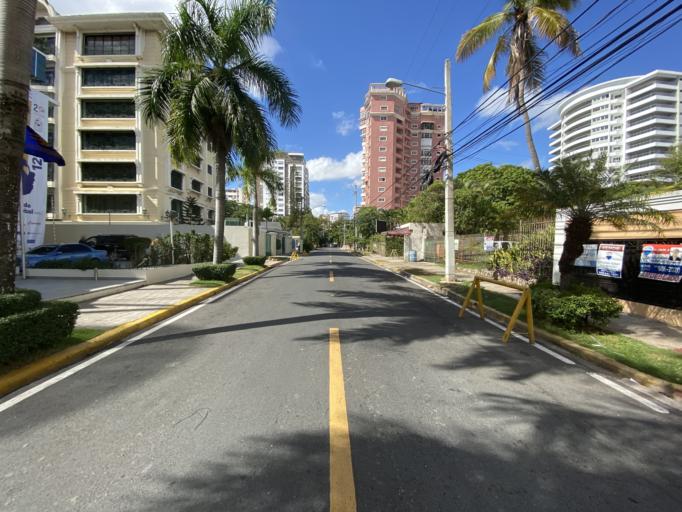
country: DO
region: Nacional
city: Ciudad Nueva
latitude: 18.4695
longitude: -69.9163
